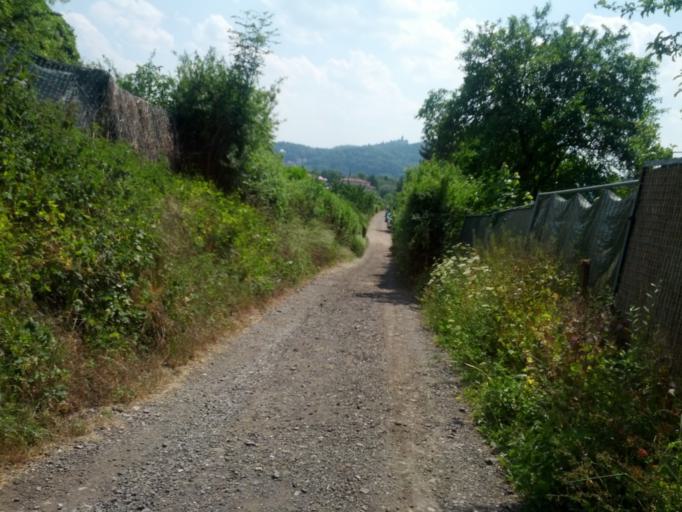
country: DE
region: Thuringia
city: Eisenach
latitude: 50.9925
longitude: 10.3196
